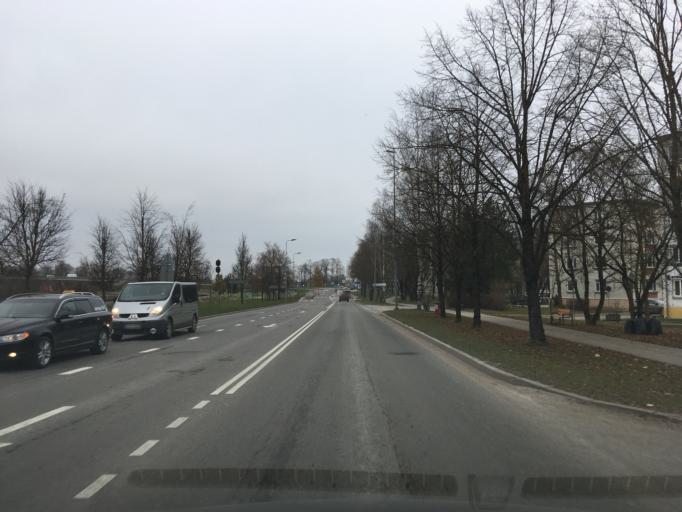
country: EE
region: Ida-Virumaa
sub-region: Johvi vald
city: Johvi
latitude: 59.3523
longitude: 27.4142
